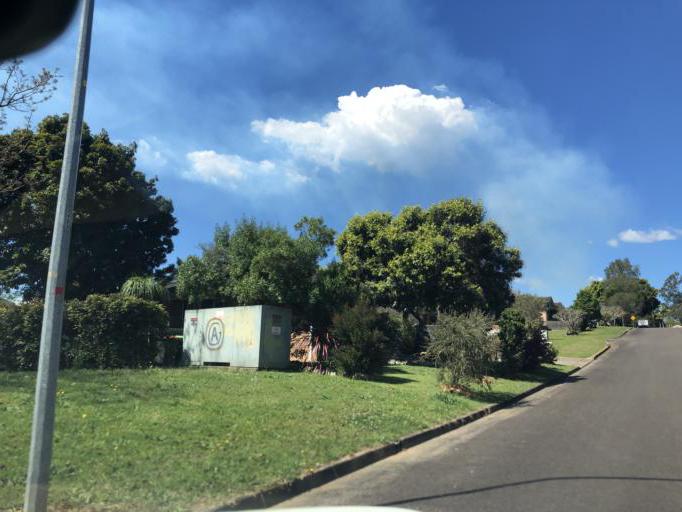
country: AU
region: New South Wales
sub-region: Bellingen
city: Bellingen
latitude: -30.4574
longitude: 152.9026
